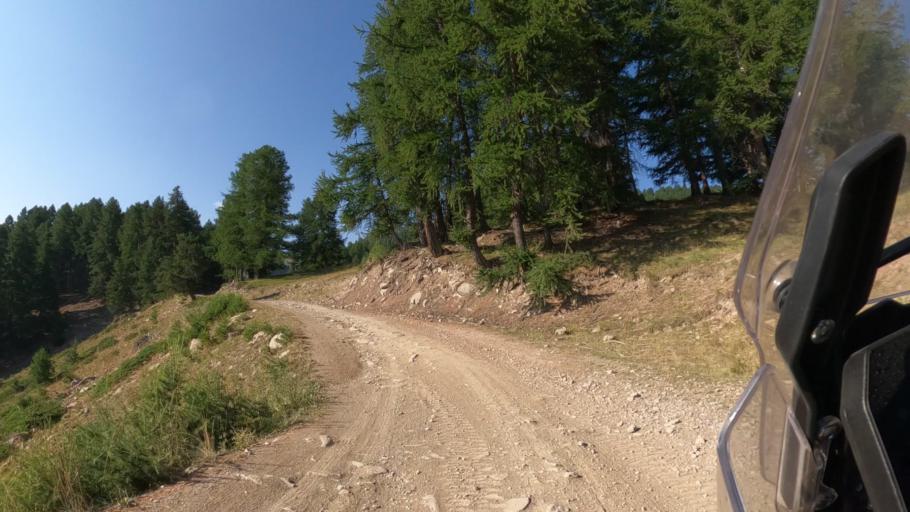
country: FR
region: Provence-Alpes-Cote d'Azur
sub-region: Departement des Hautes-Alpes
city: Guillestre
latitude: 44.6169
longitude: 6.6241
